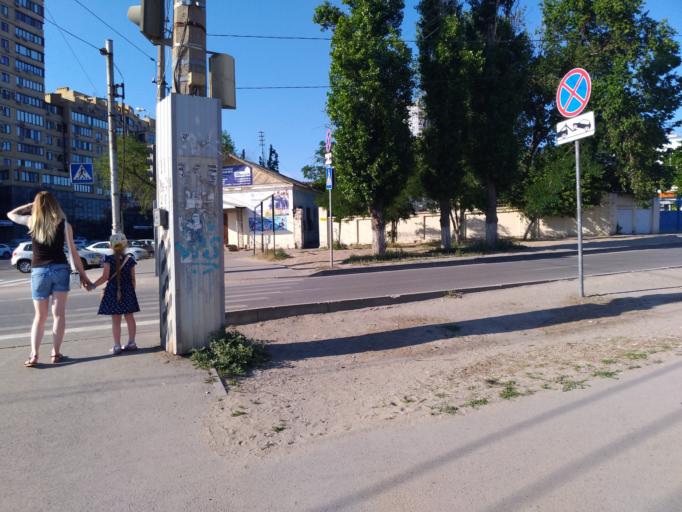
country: RU
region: Volgograd
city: Volgograd
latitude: 48.7109
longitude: 44.5038
